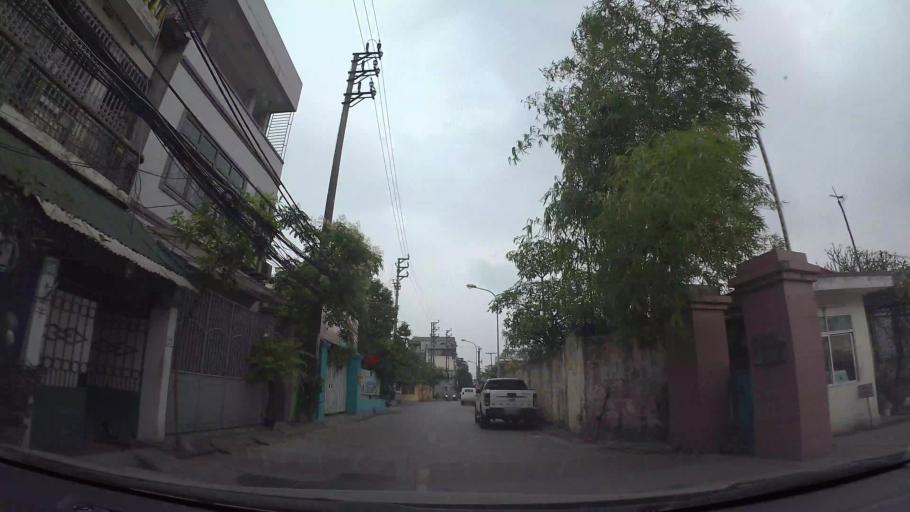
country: VN
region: Ha Noi
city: Hoan Kiem
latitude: 21.0584
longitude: 105.8946
